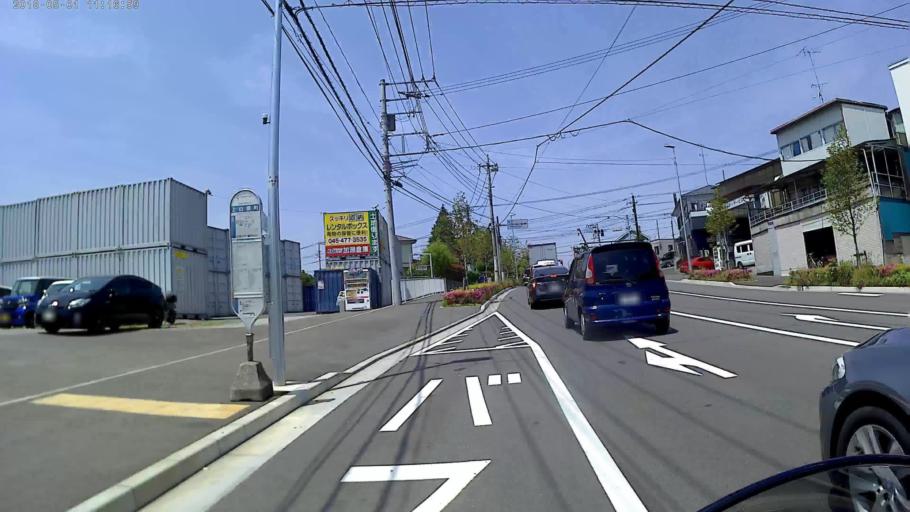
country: JP
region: Kanagawa
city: Minami-rinkan
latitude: 35.4936
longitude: 139.5338
